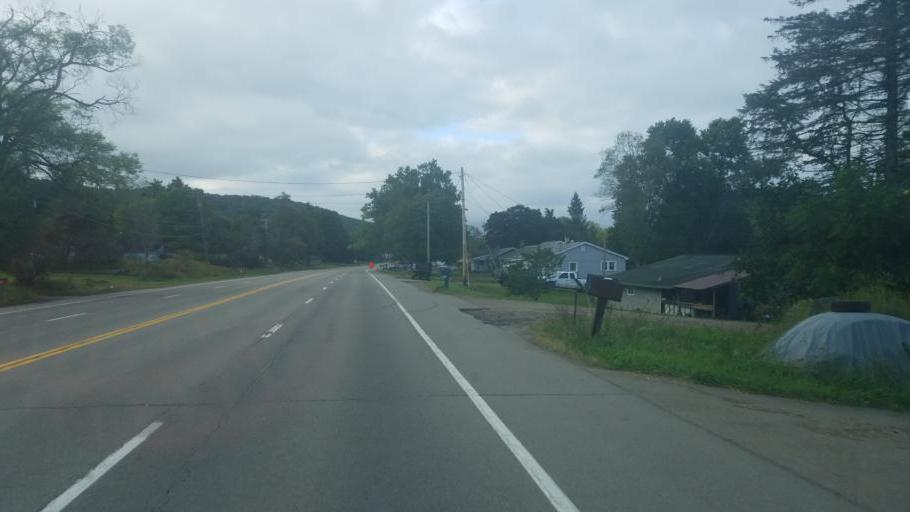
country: US
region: New York
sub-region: Cattaraugus County
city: Olean
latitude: 42.1405
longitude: -78.4011
